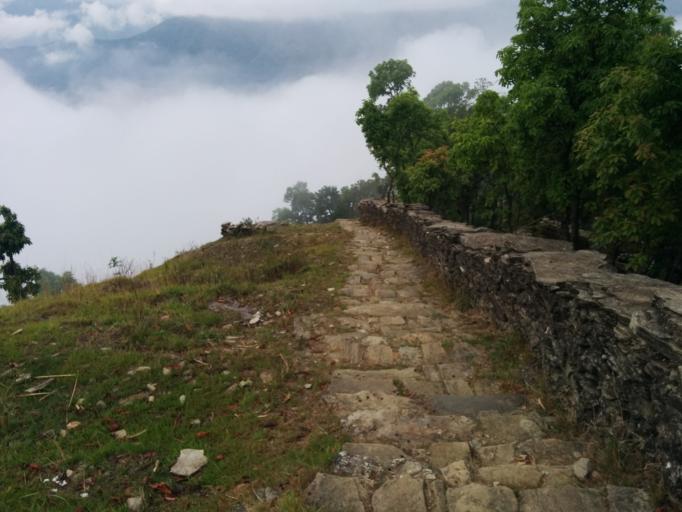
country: NP
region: Western Region
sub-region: Gandaki Zone
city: Pokhara
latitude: 28.2365
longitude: 83.9493
